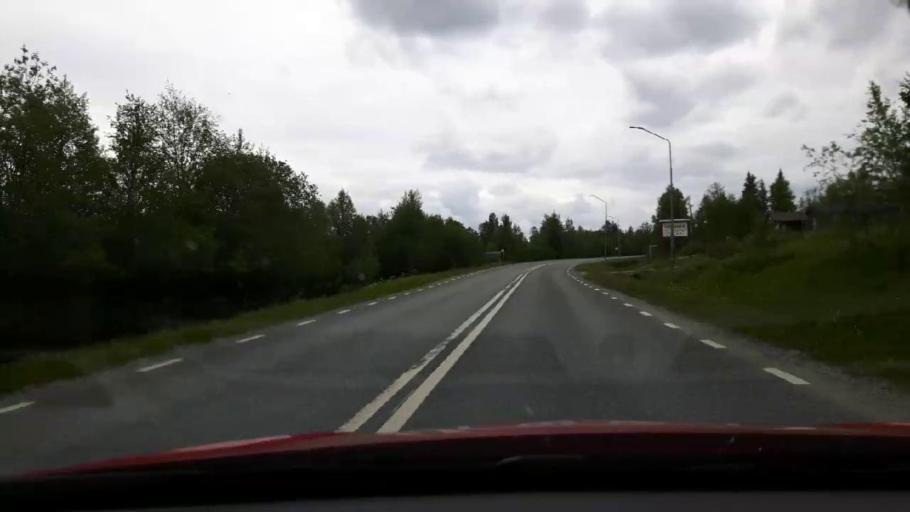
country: NO
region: Hedmark
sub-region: Engerdal
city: Engerdal
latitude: 62.5437
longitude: 12.4689
